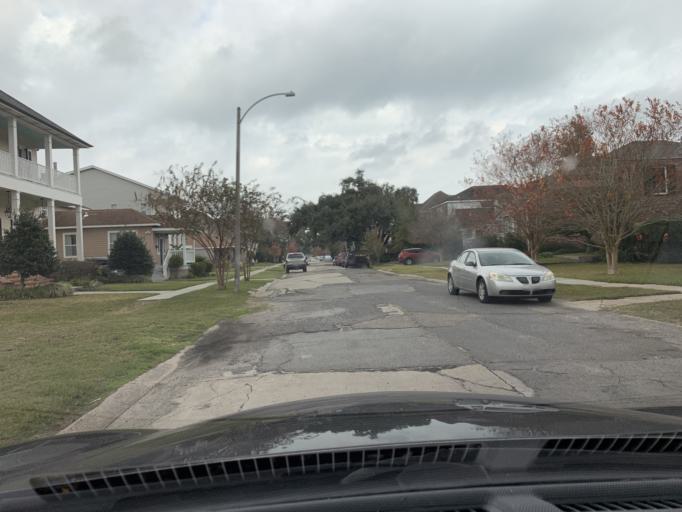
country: US
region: Louisiana
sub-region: Jefferson Parish
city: Metairie
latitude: 30.0157
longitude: -90.1002
